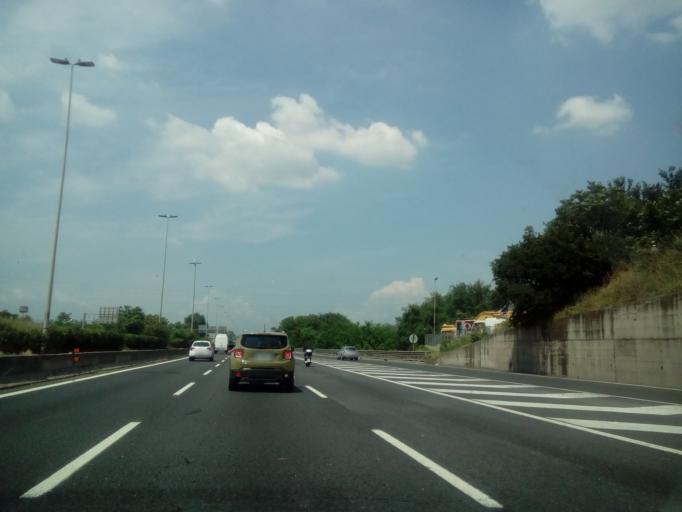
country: IT
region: Latium
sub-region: Citta metropolitana di Roma Capitale
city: Setteville
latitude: 41.8956
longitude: 12.6154
